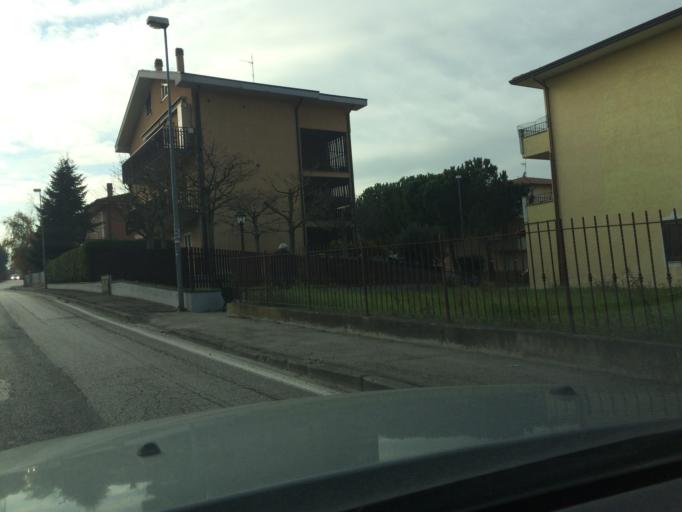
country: IT
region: Umbria
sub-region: Provincia di Perugia
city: Via Lippia
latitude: 43.0871
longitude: 12.4800
